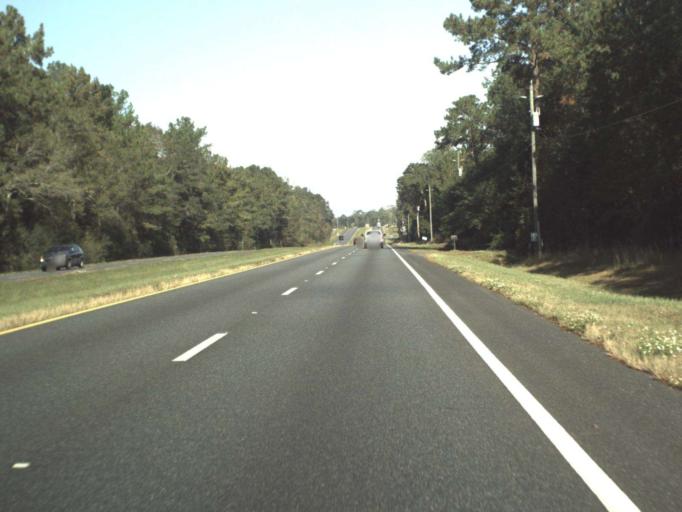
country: US
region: Florida
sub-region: Gadsden County
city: Havana
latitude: 30.5804
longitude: -84.3993
